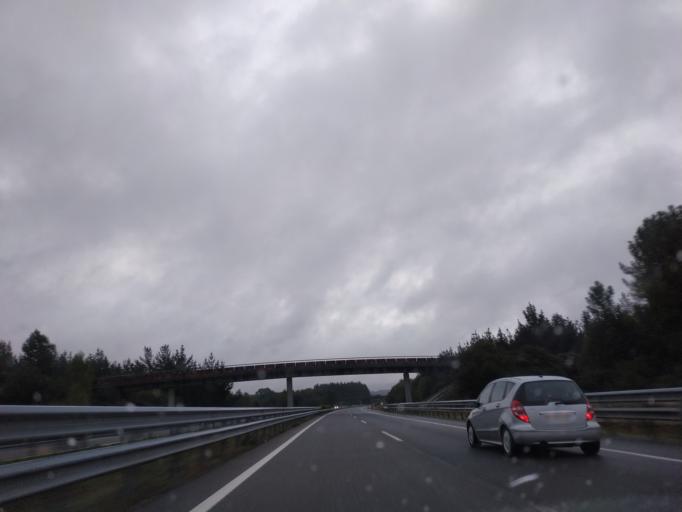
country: ES
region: Galicia
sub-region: Provincia de Lugo
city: Outeiro de Rei
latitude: 43.0884
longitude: -7.5844
